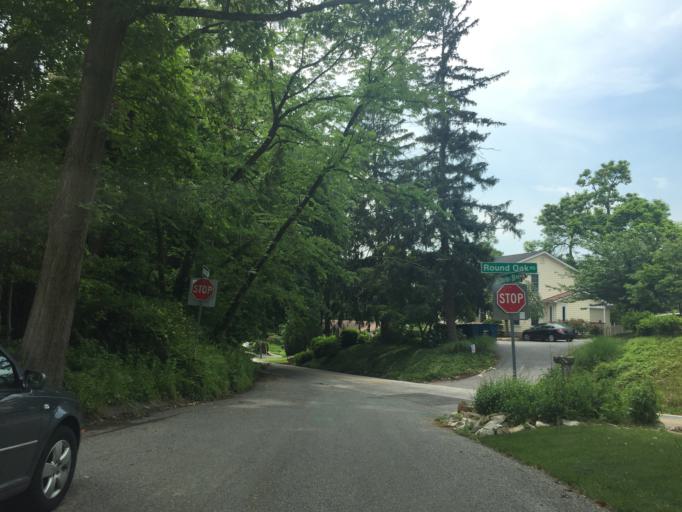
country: US
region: Maryland
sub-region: Baltimore County
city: Towson
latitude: 39.4047
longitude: -76.6187
